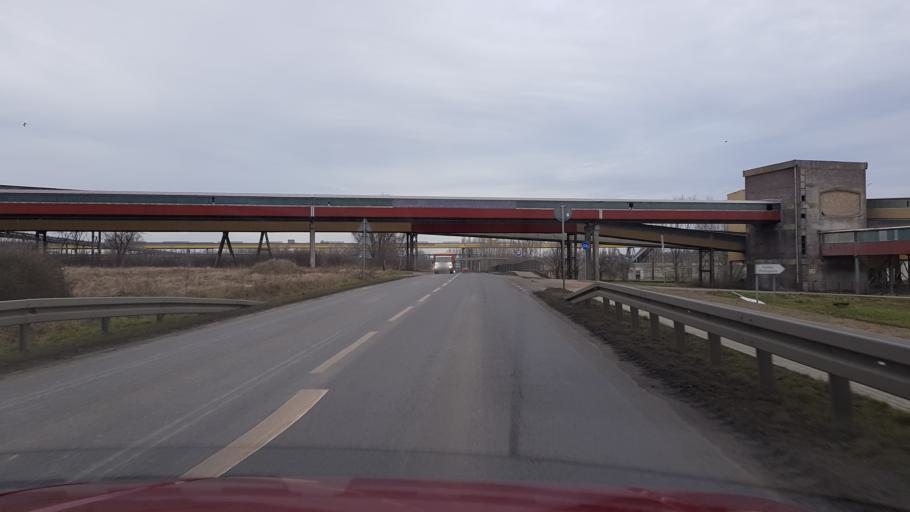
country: PL
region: West Pomeranian Voivodeship
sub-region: Powiat policki
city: Police
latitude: 53.5730
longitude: 14.5560
